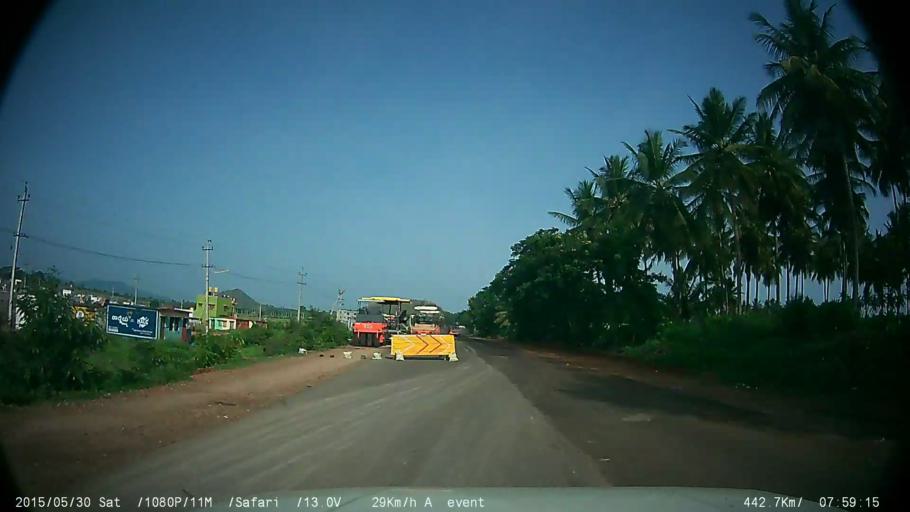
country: IN
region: Karnataka
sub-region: Chamrajnagar
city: Gundlupet
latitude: 11.8040
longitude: 76.6815
